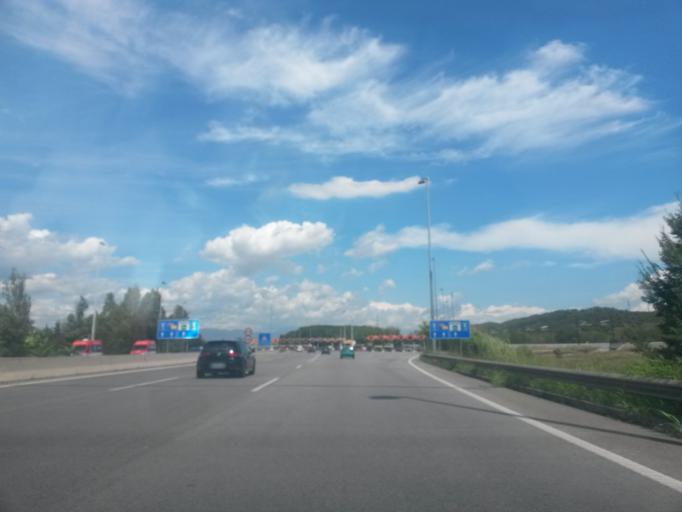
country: ES
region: Catalonia
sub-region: Provincia de Barcelona
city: La Llagosta
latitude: 41.5073
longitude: 2.2020
